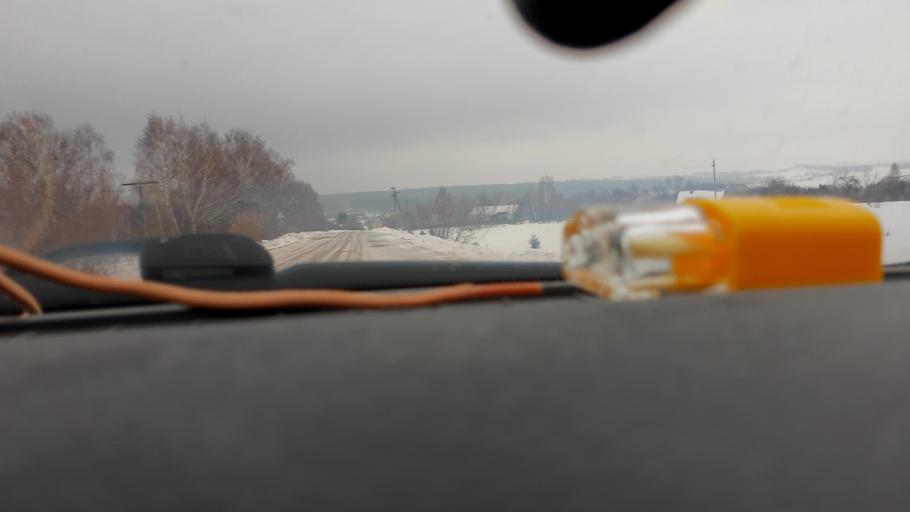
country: RU
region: Bashkortostan
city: Ulukulevo
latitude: 54.6107
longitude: 56.4223
